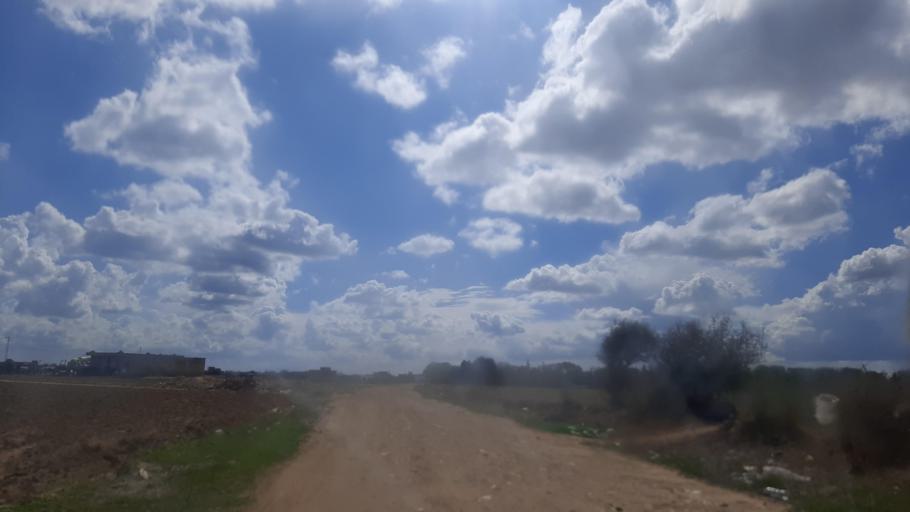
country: TN
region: Nabul
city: Korba
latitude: 36.5992
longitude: 10.8564
